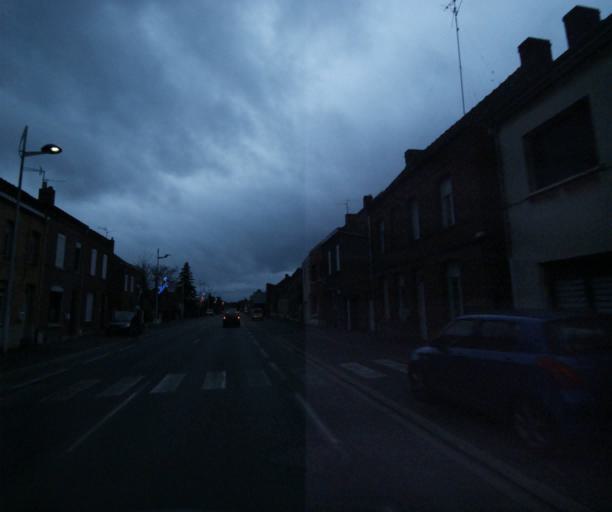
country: FR
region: Nord-Pas-de-Calais
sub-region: Departement du Nord
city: Beuvrages
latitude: 50.3983
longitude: 3.4943
